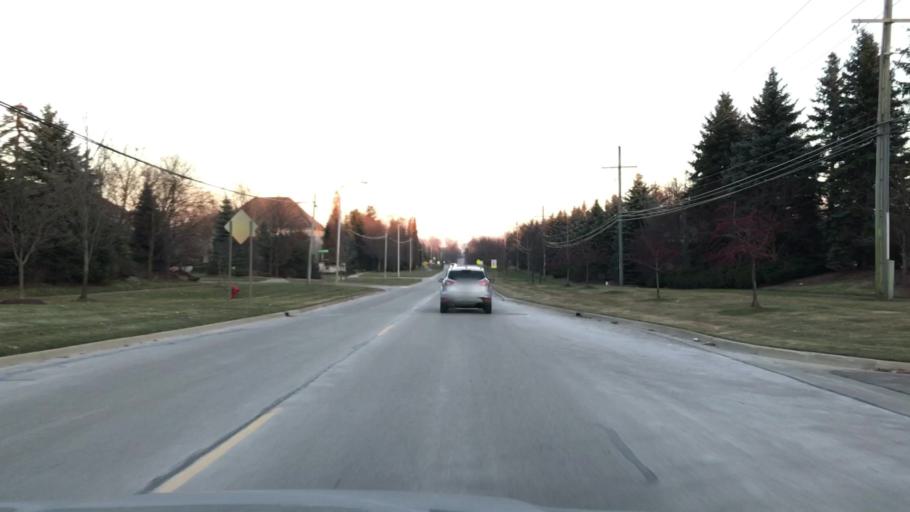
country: US
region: Michigan
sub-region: Wayne County
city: Northville
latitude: 42.4510
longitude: -83.5100
